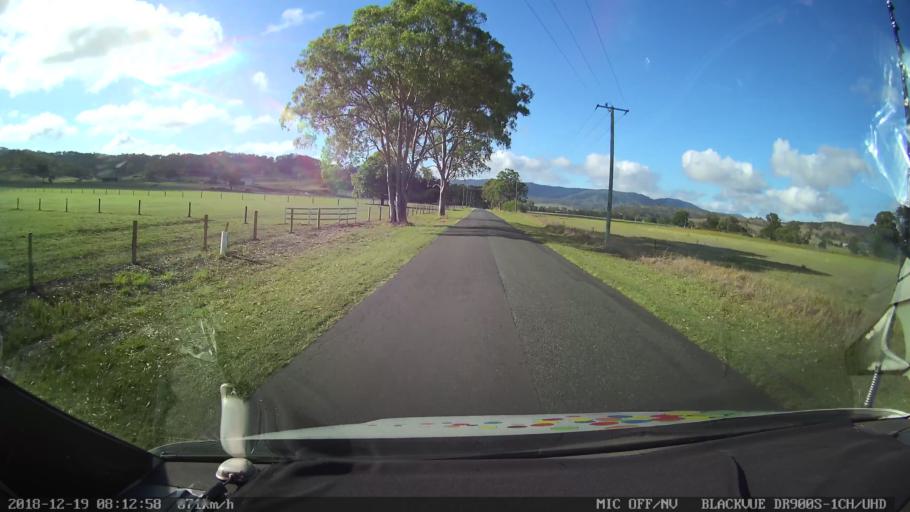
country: AU
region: Queensland
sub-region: Logan
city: Cedar Vale
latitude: -28.2335
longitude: 152.8914
